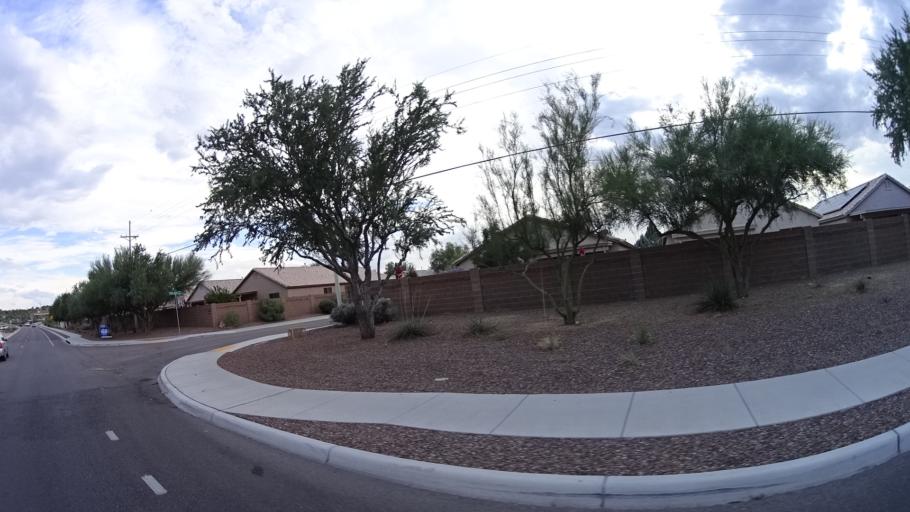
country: US
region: Arizona
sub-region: Pima County
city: Casas Adobes
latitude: 32.3505
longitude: -111.0282
